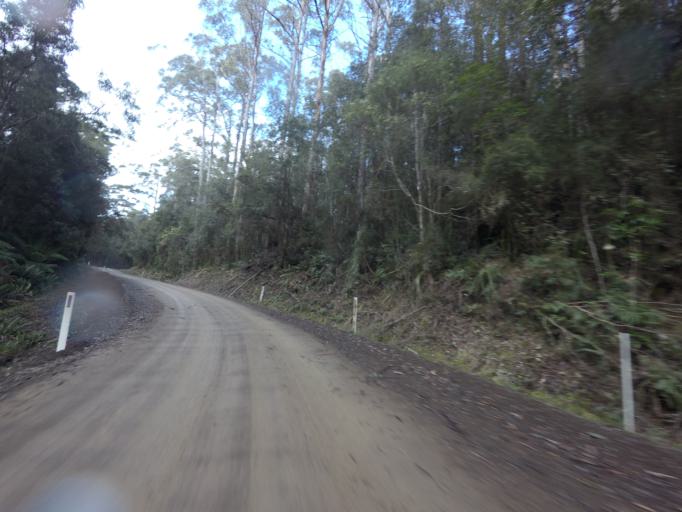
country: AU
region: Tasmania
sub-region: Huon Valley
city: Geeveston
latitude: -43.5746
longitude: 146.8876
